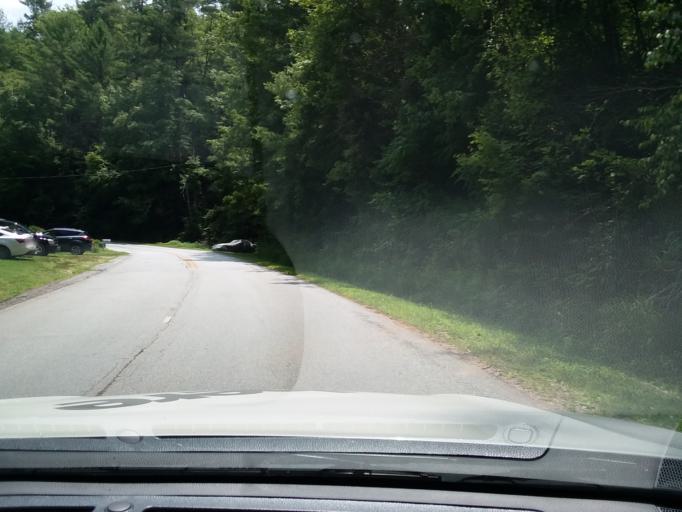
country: US
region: Georgia
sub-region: Rabun County
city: Mountain City
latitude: 34.9798
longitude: -83.1869
